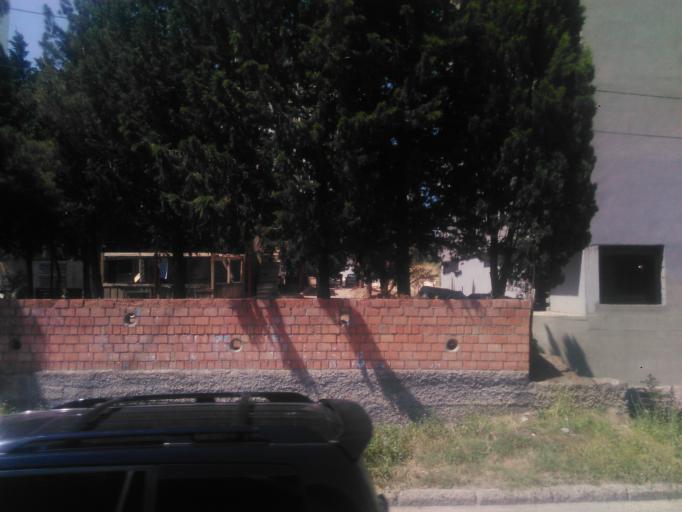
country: GE
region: T'bilisi
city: Tbilisi
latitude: 41.7053
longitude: 44.8853
